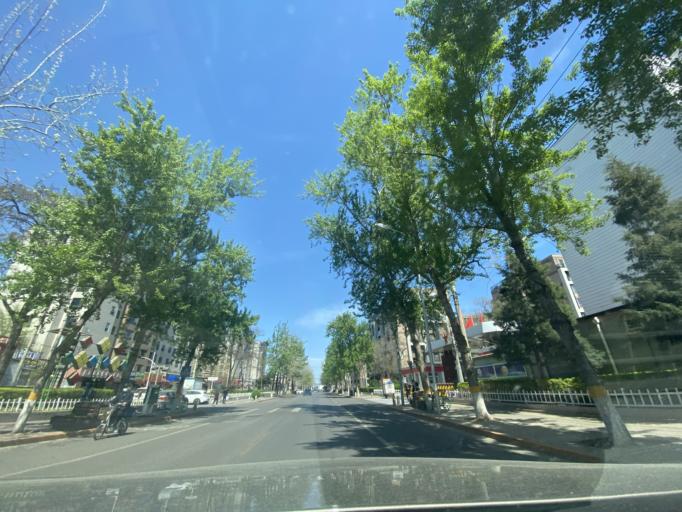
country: CN
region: Beijing
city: Sijiqing
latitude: 39.9250
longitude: 116.2587
